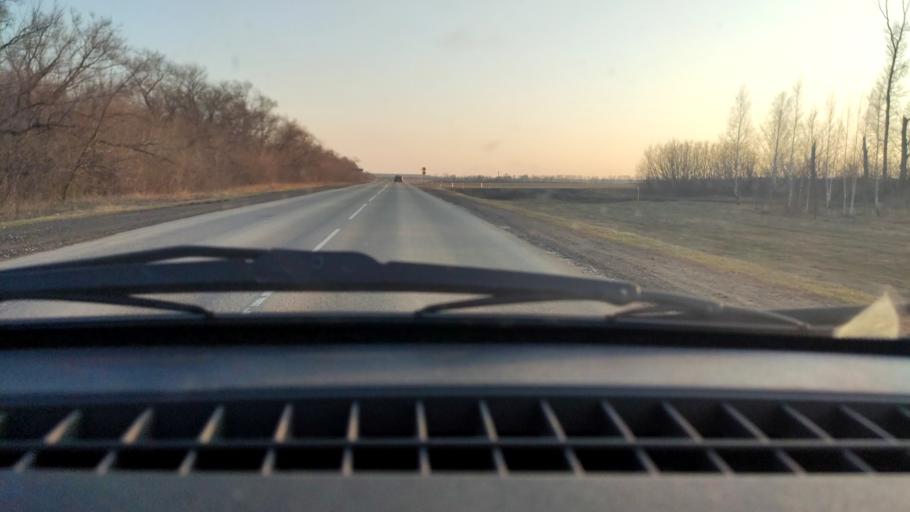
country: RU
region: Bashkortostan
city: Davlekanovo
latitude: 54.2884
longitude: 55.1179
